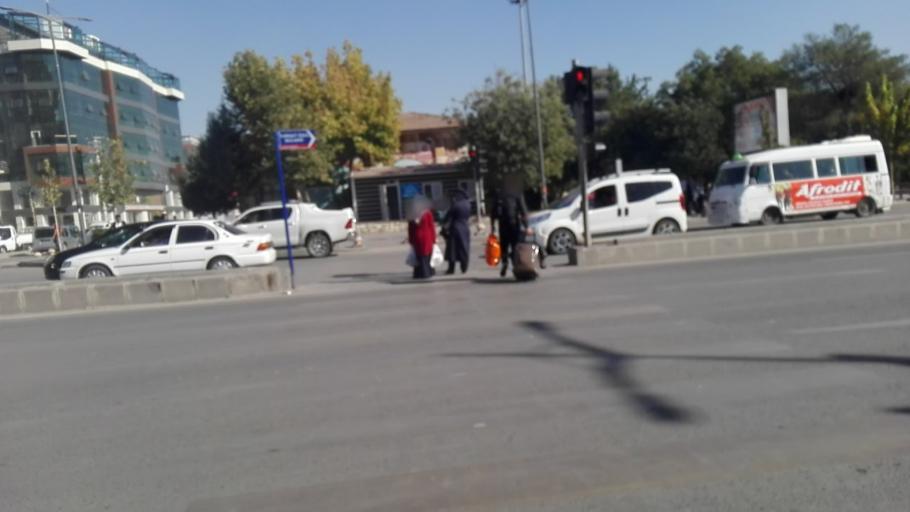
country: TR
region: Batman
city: Batman
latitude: 37.8962
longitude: 41.1302
